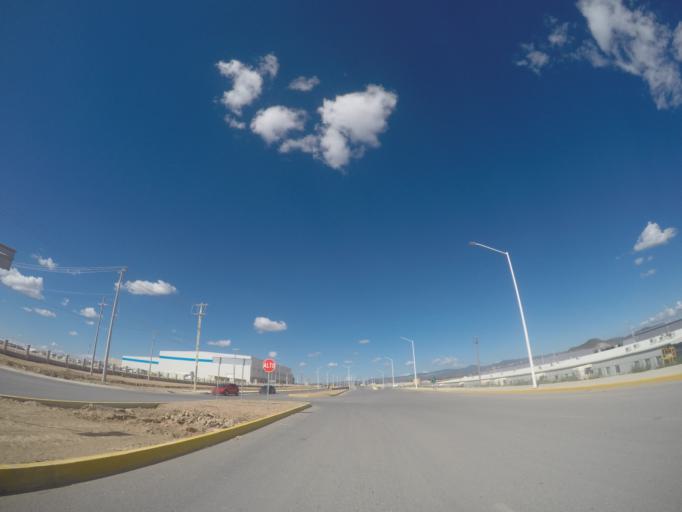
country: MX
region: San Luis Potosi
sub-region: Zaragoza
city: Cerro Gordo
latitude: 21.9743
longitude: -100.8533
